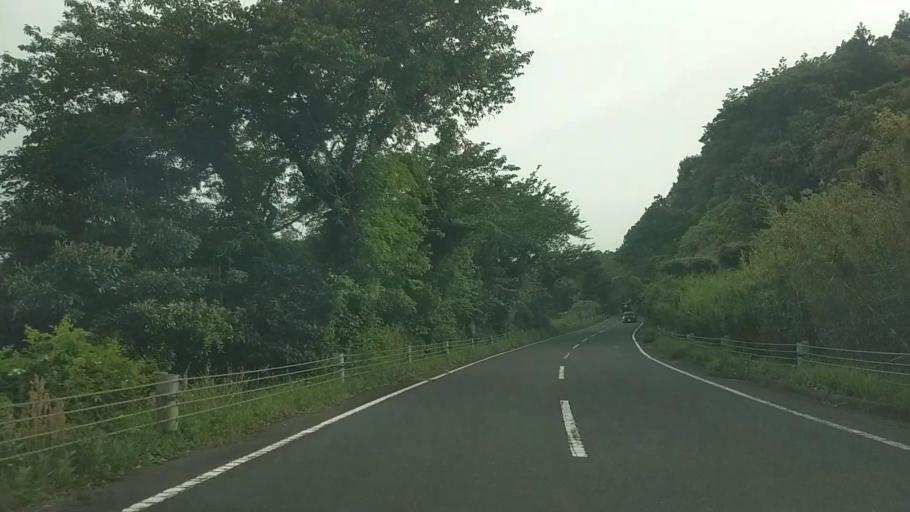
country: JP
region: Shizuoka
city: Kosai-shi
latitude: 34.7454
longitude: 137.5991
